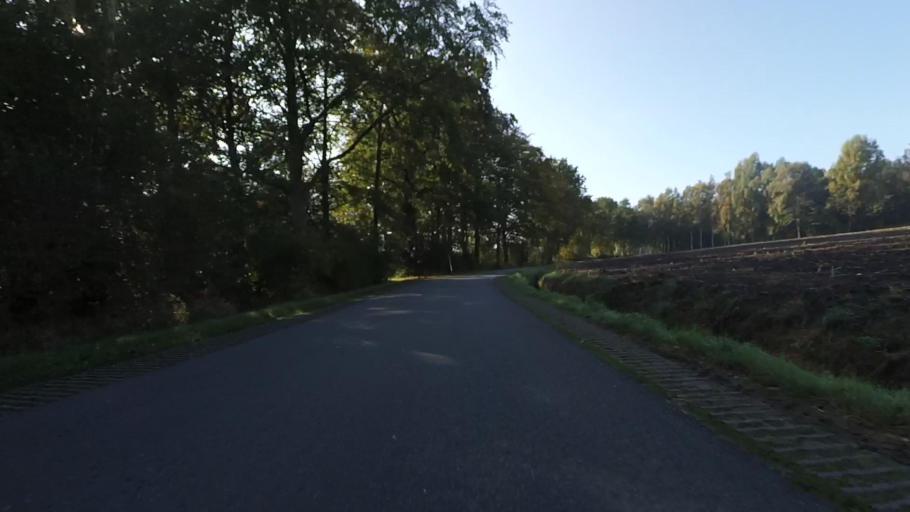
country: NL
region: Gelderland
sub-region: Gemeente Nijkerk
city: Nijkerk
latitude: 52.2348
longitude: 5.5449
